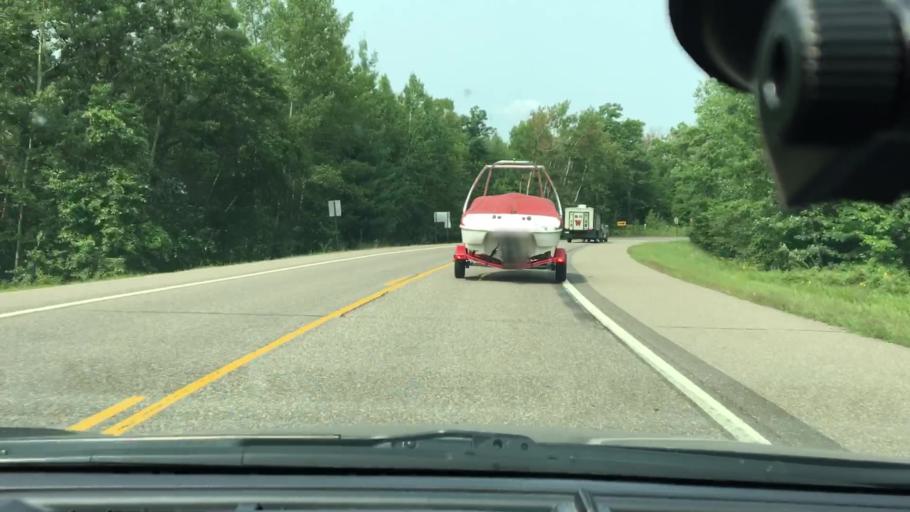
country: US
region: Minnesota
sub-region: Cass County
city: East Gull Lake
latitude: 46.4072
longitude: -94.3553
